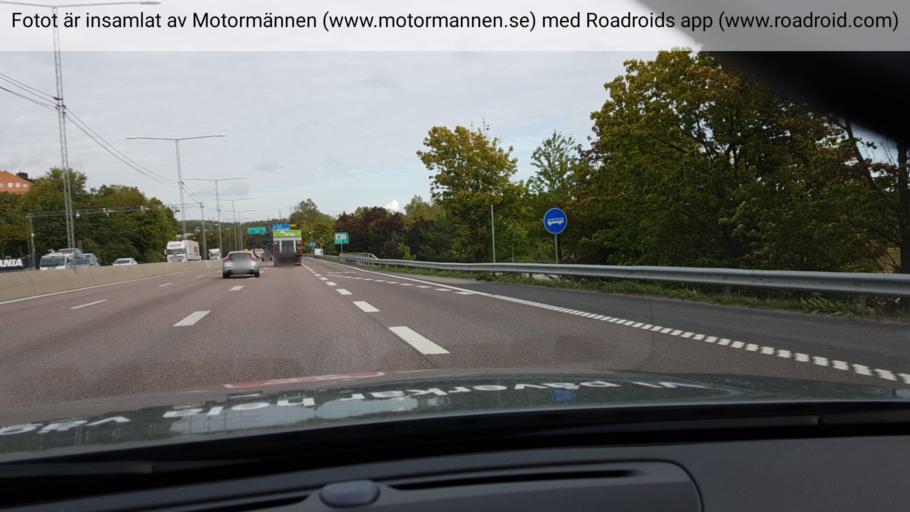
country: SE
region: Stockholm
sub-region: Danderyds Kommun
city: Djursholm
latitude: 59.4028
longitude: 18.0372
